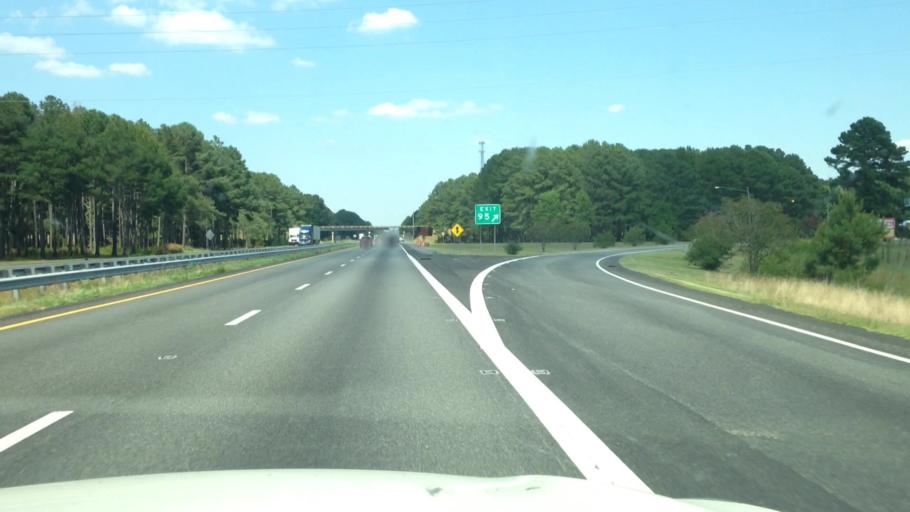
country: US
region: North Carolina
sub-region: Johnston County
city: Smithfield
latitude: 35.5019
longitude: -78.3252
